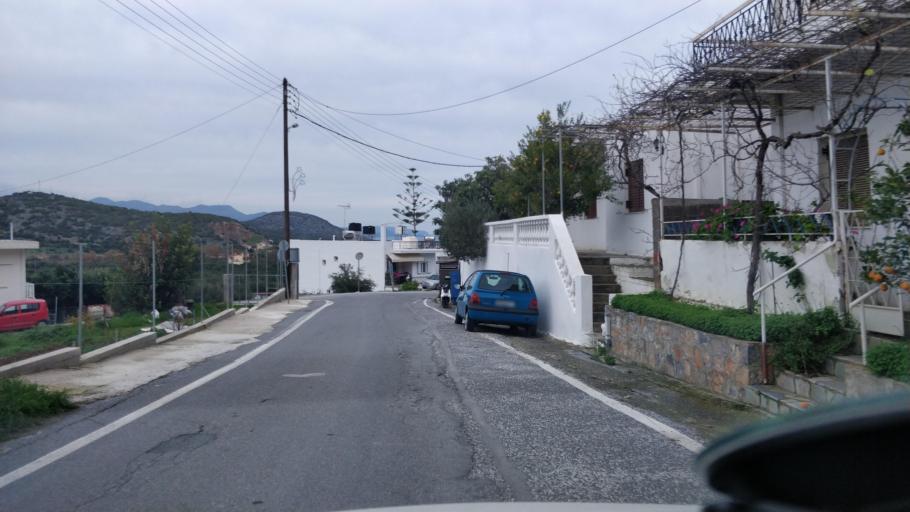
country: GR
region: Crete
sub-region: Nomos Lasithiou
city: Agios Nikolaos
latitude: 35.1162
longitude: 25.7261
